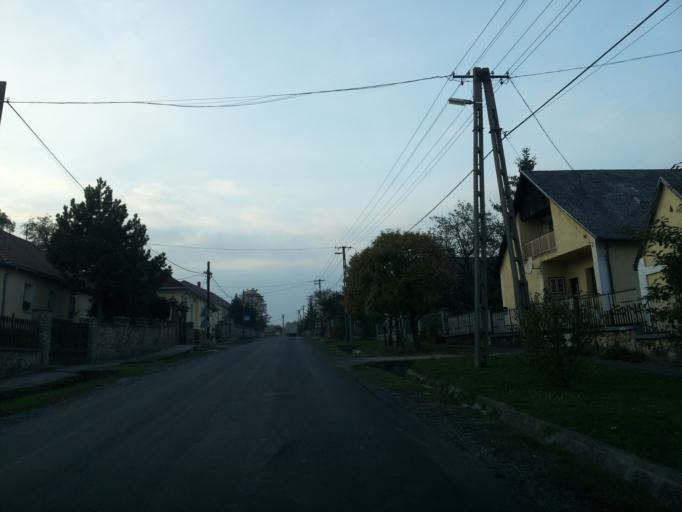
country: HU
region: Gyor-Moson-Sopron
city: Bakonyszentlaszlo
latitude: 47.4671
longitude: 17.9034
